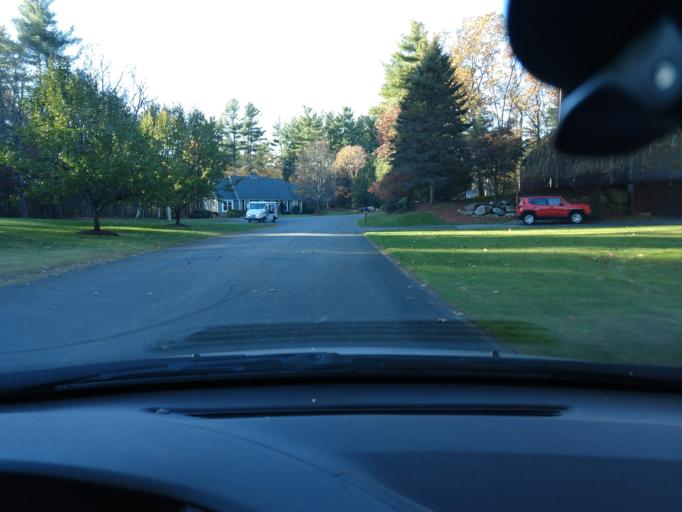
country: US
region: Massachusetts
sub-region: Middlesex County
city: Westford
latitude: 42.5386
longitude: -71.4171
